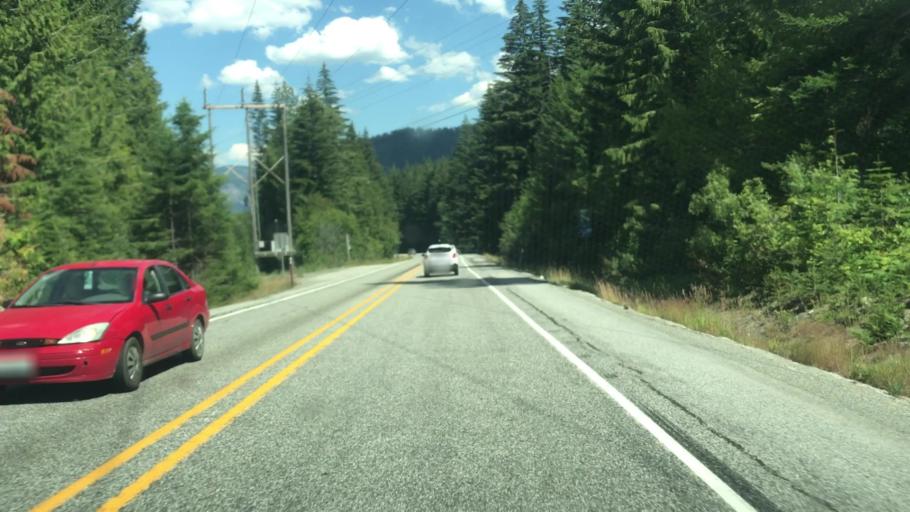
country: US
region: Washington
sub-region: Chelan County
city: Leavenworth
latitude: 47.7711
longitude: -120.9802
